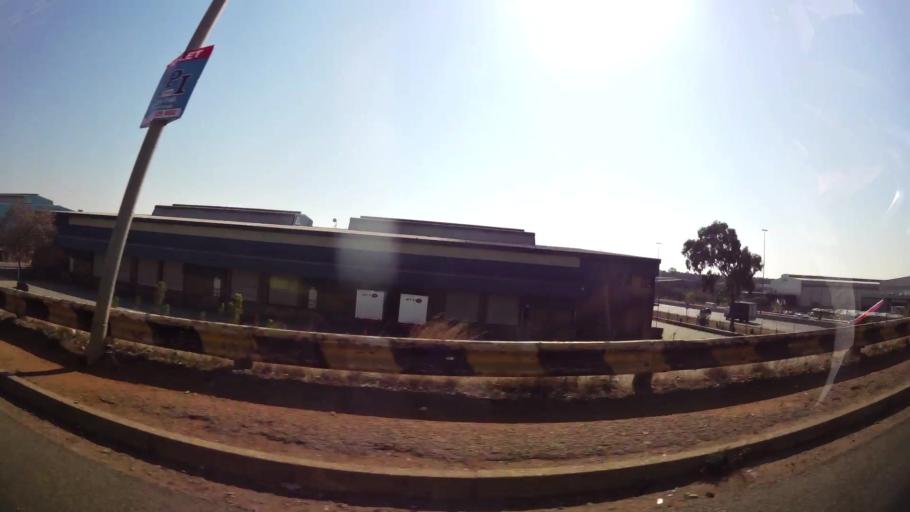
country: ZA
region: Gauteng
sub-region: Ekurhuleni Metropolitan Municipality
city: Boksburg
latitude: -26.1682
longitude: 28.2289
